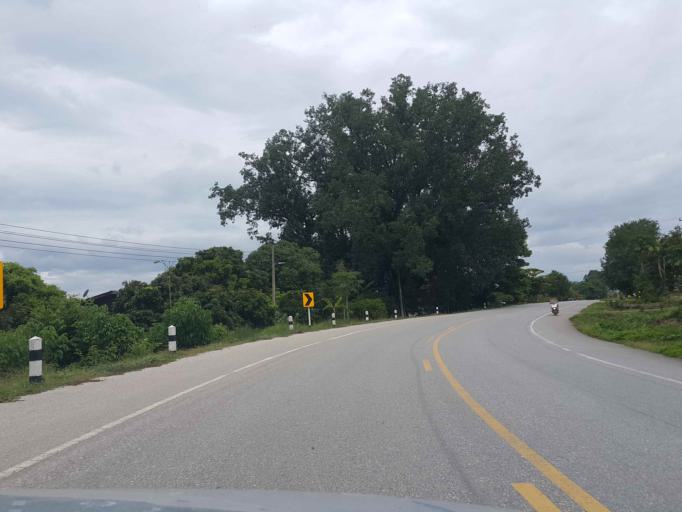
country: TH
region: Lamphun
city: Li
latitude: 17.7416
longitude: 99.0254
